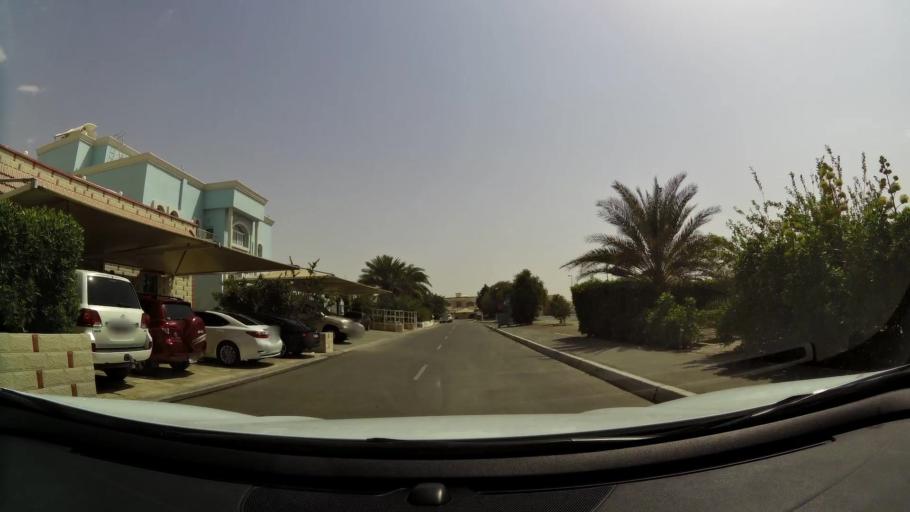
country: AE
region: Abu Dhabi
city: Abu Dhabi
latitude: 24.2938
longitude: 54.6463
